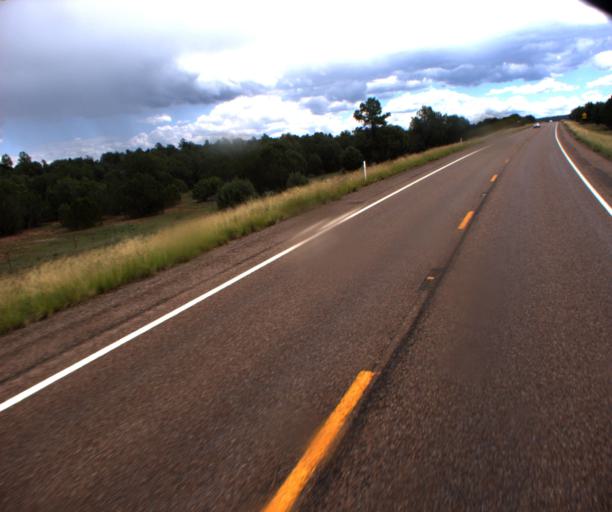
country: US
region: Arizona
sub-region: Navajo County
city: Linden
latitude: 34.3608
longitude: -110.3238
